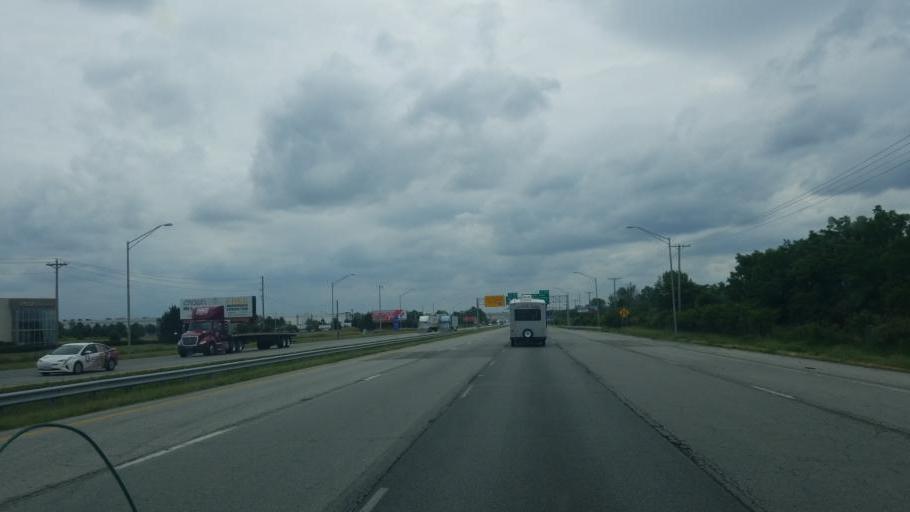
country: US
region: Indiana
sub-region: Hendricks County
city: Plainfield
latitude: 39.6729
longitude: -86.3578
